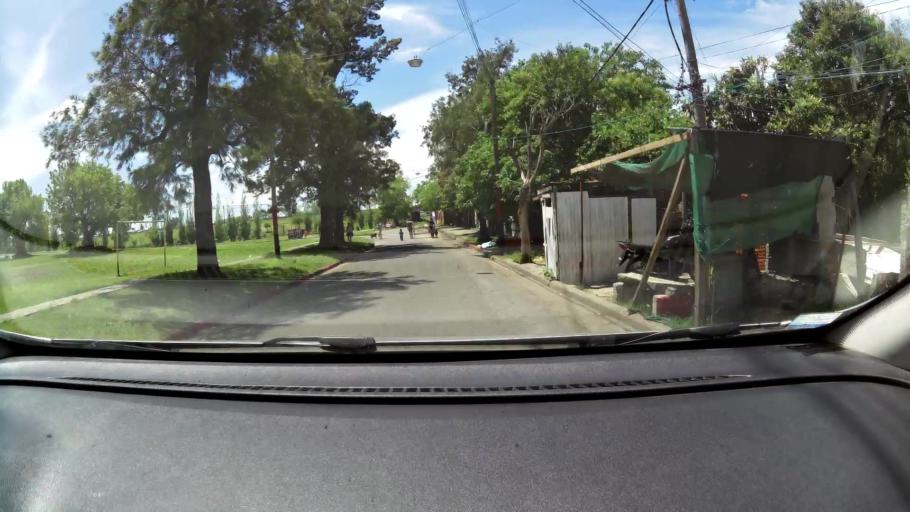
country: AR
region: Santa Fe
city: Gobernador Galvez
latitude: -32.9961
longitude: -60.6199
